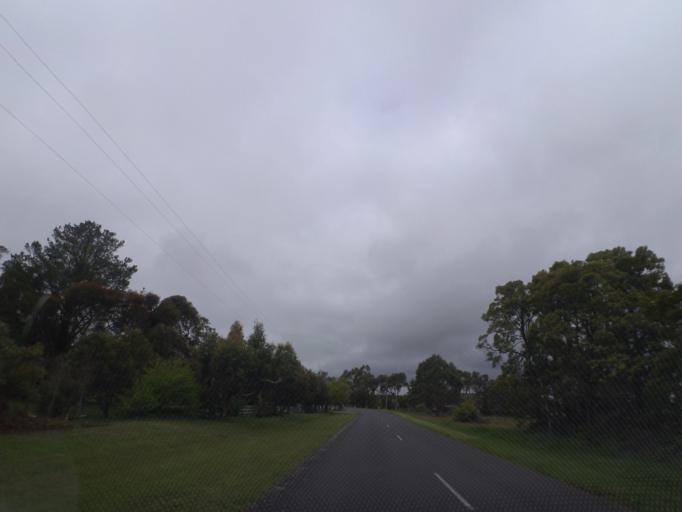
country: AU
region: Victoria
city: Brown Hill
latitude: -37.5977
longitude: 144.1019
